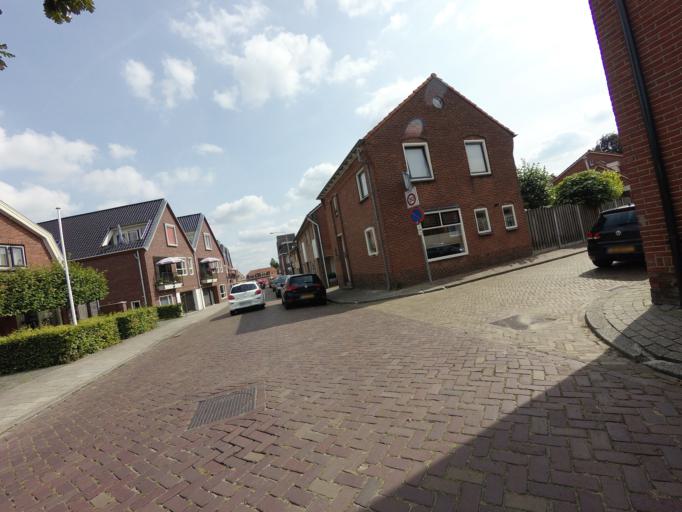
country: DE
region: Lower Saxony
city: Getelo
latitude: 52.4094
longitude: 6.8964
